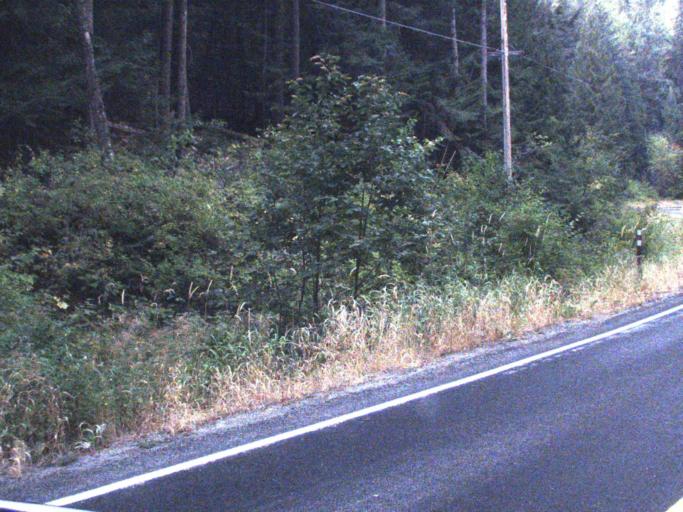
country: US
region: Washington
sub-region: Spokane County
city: Trentwood
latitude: 47.8354
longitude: -117.1817
